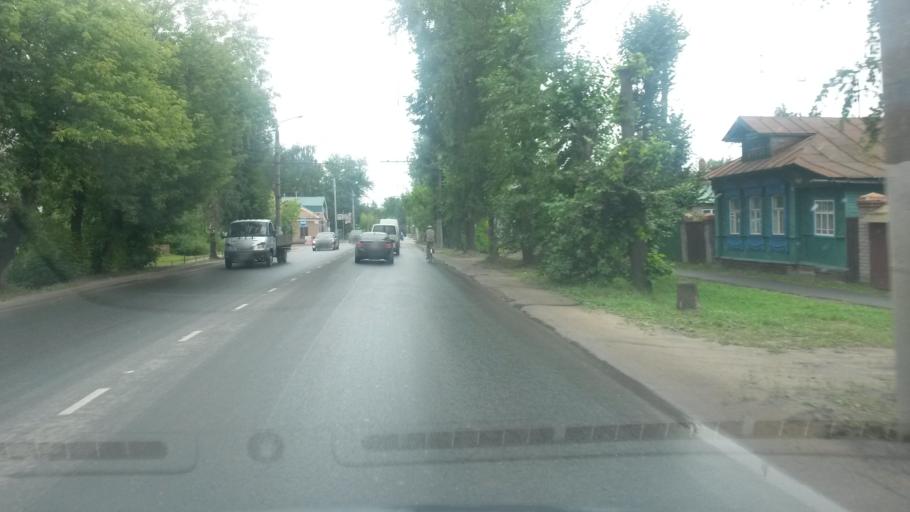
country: RU
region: Ivanovo
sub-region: Gorod Ivanovo
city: Ivanovo
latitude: 57.0127
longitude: 40.9359
